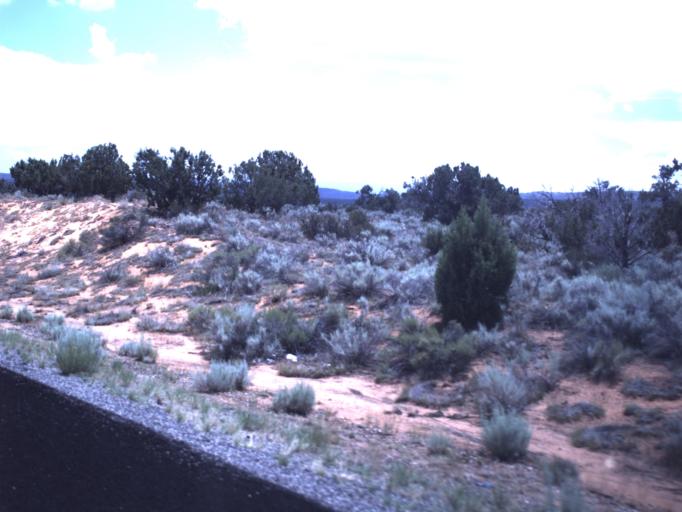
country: US
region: Utah
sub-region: Kane County
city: Kanab
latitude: 37.1576
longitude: -112.5804
